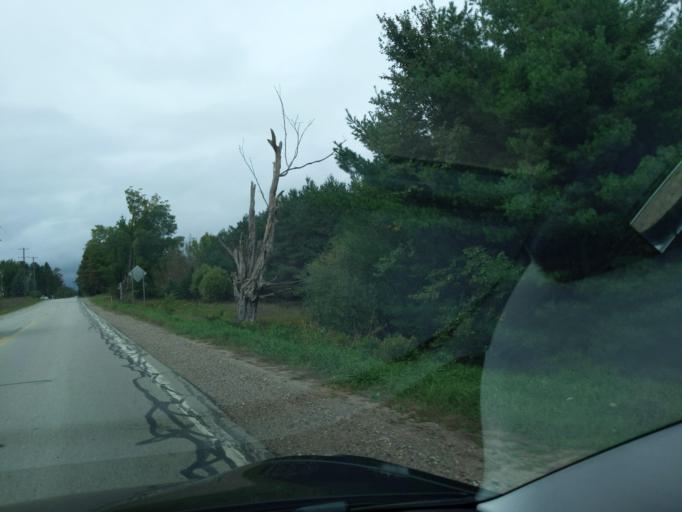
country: US
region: Michigan
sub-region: Wexford County
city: Manton
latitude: 44.5873
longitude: -85.3529
